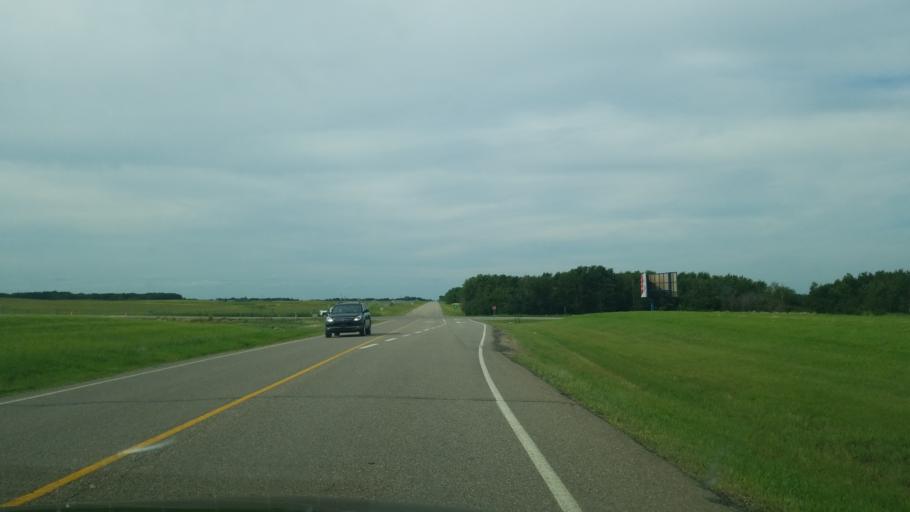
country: CA
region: Saskatchewan
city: Lloydminster
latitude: 53.3060
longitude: -110.0543
